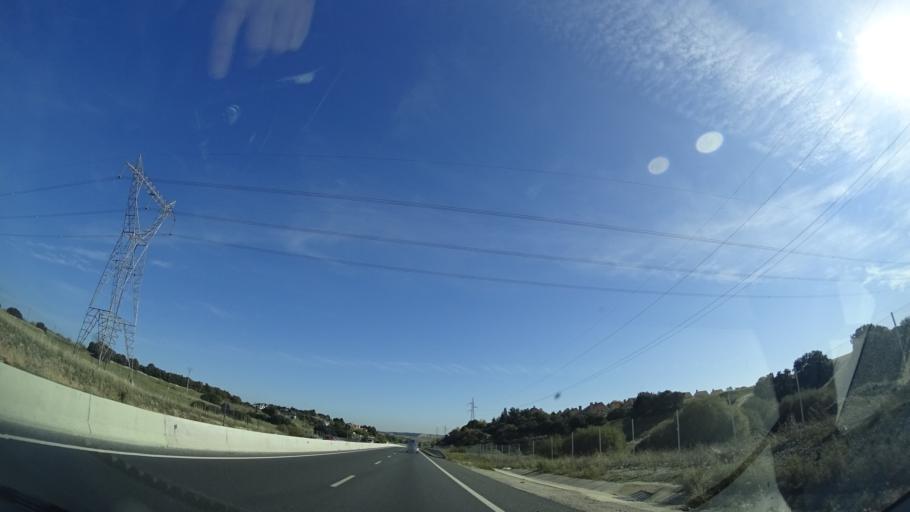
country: ES
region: Madrid
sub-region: Provincia de Madrid
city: Villanueva del Pardillo
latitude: 40.4906
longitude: -3.9535
